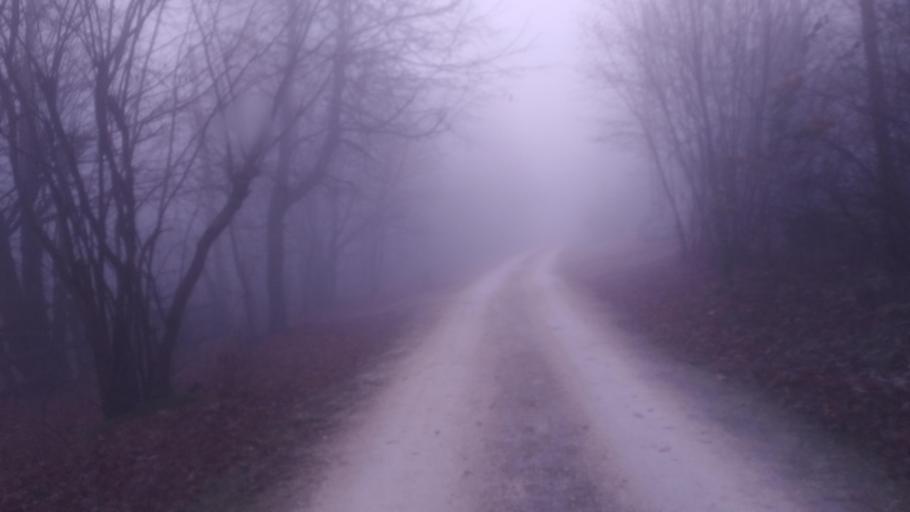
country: HU
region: Pest
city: Pilisszentkereszt
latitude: 47.7166
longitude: 18.8936
